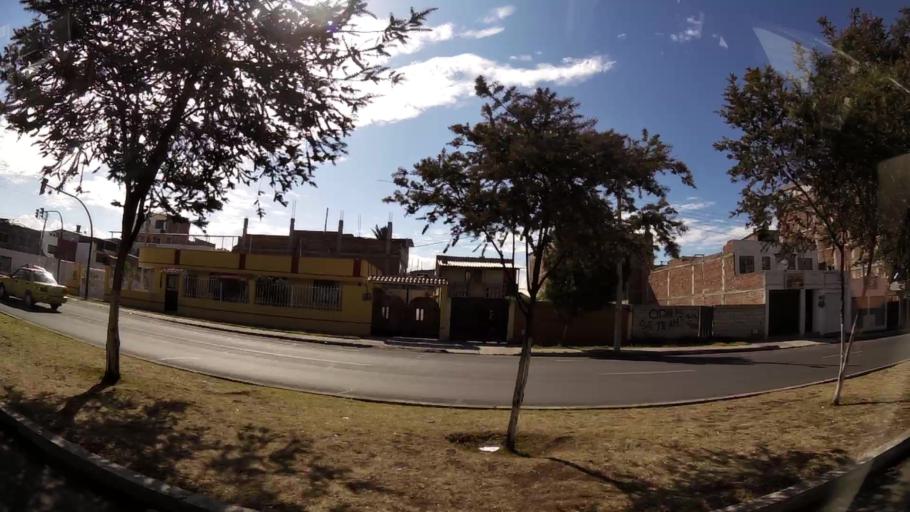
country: EC
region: Chimborazo
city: Riobamba
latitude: -1.6553
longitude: -78.6701
